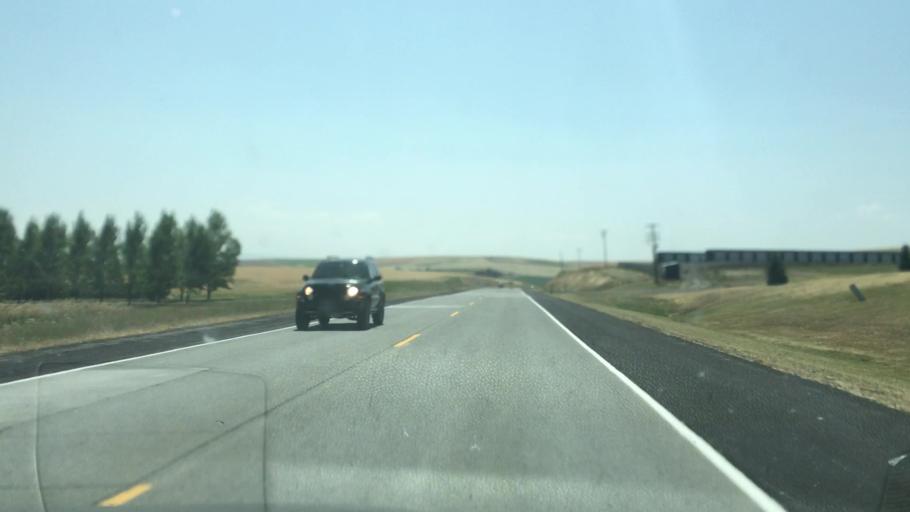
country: US
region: Idaho
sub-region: Lewis County
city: Nezperce
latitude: 46.0781
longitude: -116.3435
